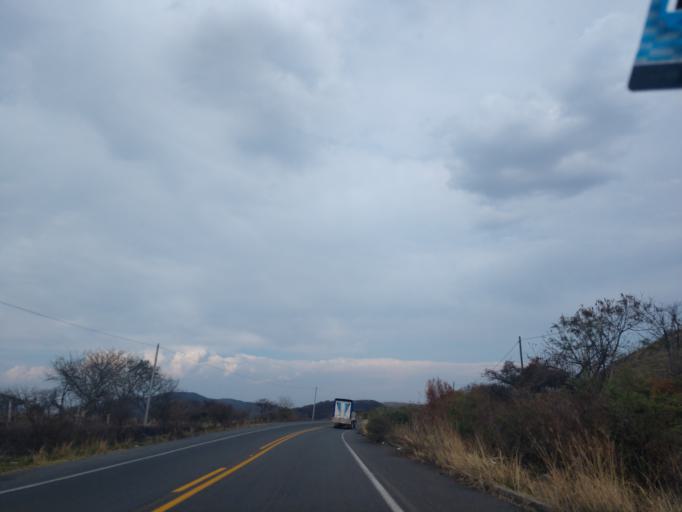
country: MX
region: Jalisco
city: La Manzanilla de la Paz
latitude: 20.1206
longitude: -103.1628
